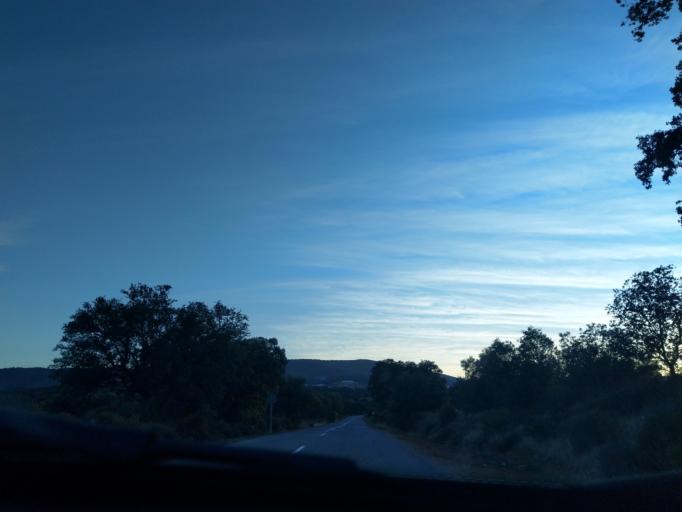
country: ES
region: Extremadura
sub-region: Provincia de Badajoz
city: Valverde de Llerena
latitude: 38.1728
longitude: -5.8744
